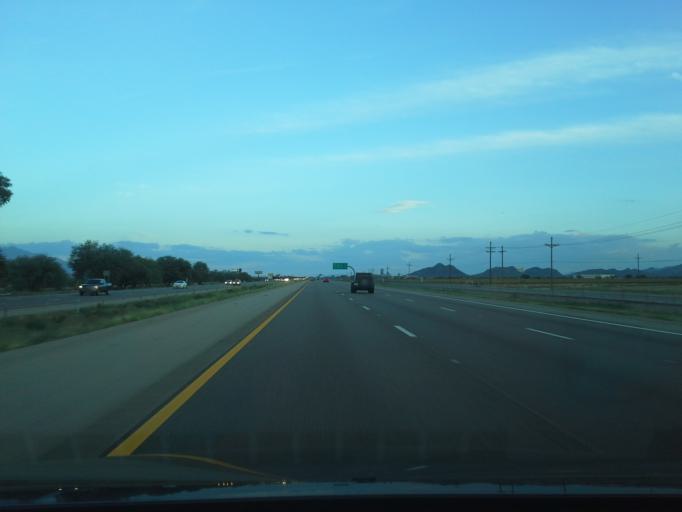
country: US
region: Arizona
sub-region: Pima County
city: Marana
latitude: 32.4389
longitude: -111.1841
